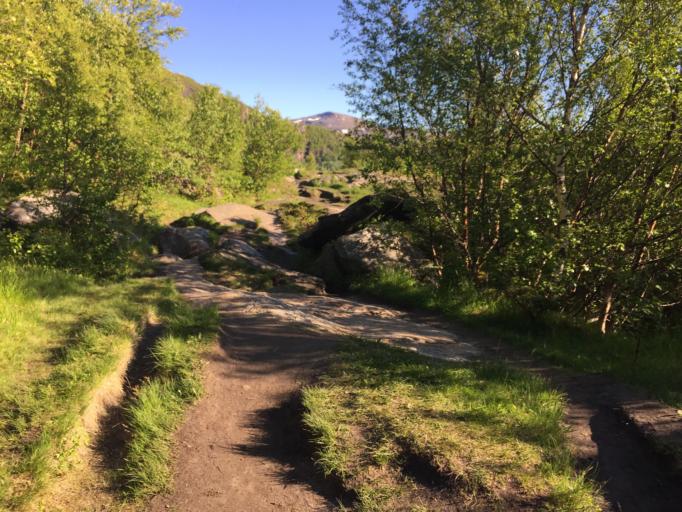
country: NO
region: Nordland
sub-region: Bodo
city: Loding
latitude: 67.4163
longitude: 14.6326
